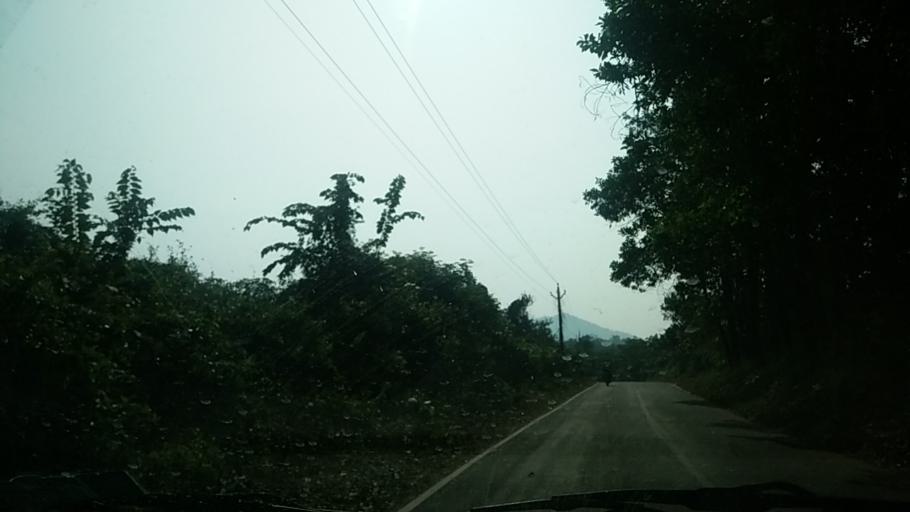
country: IN
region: Goa
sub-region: South Goa
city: Sanguem
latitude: 15.2261
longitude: 74.1882
